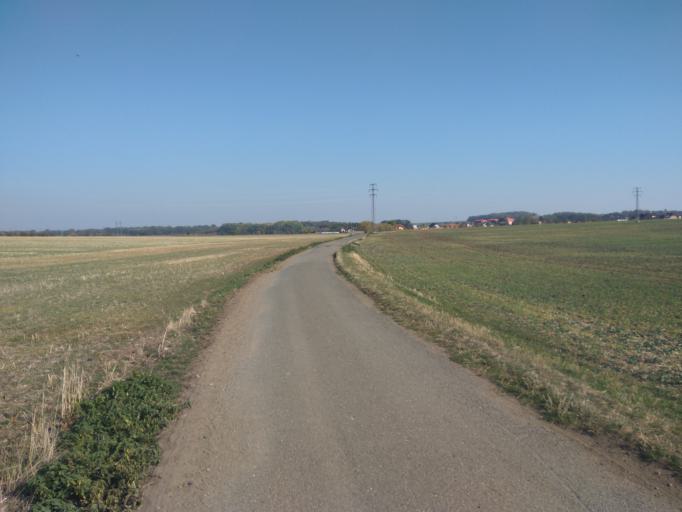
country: CZ
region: Central Bohemia
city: Hovorcovice
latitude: 50.1778
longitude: 14.5386
